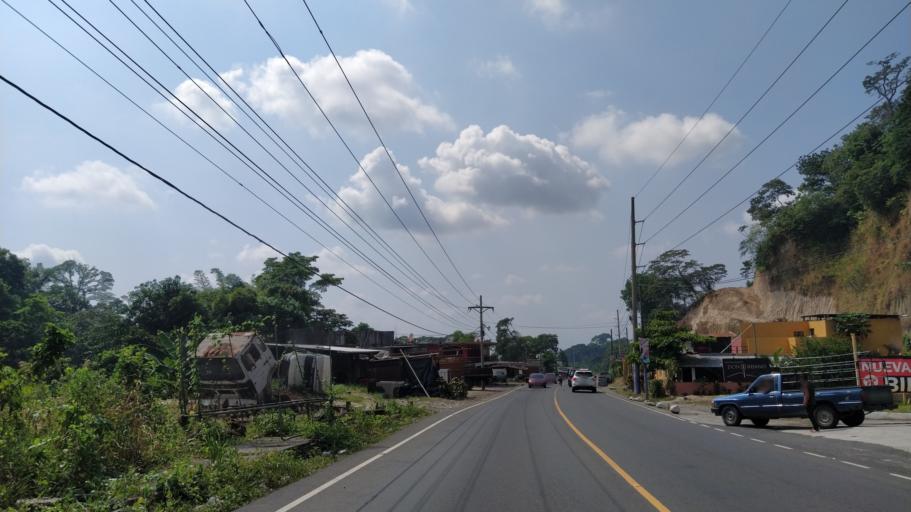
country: GT
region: Quetzaltenango
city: El Palmar
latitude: 14.6431
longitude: -91.5733
